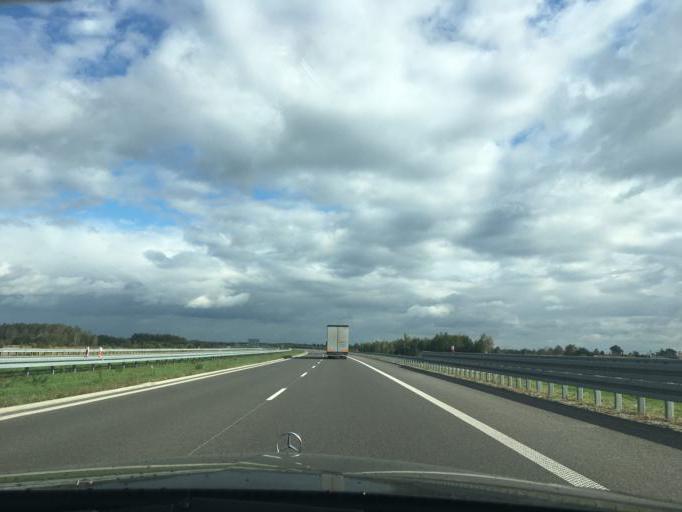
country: PL
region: Subcarpathian Voivodeship
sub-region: Powiat rzeszowski
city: Krasne
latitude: 50.0924
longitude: 22.0777
